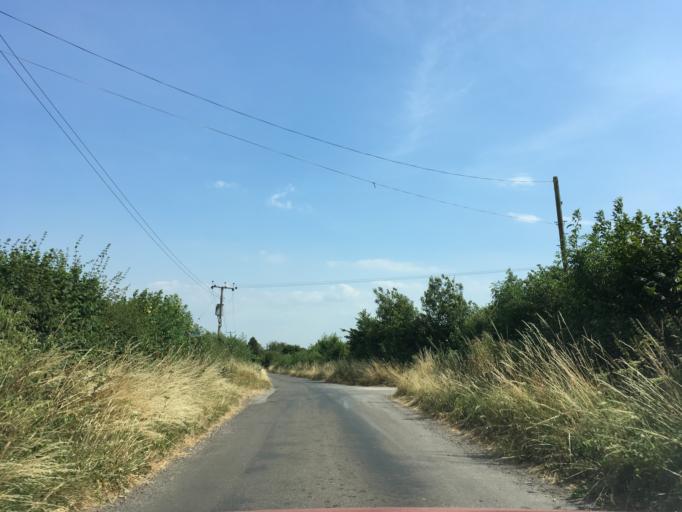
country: GB
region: England
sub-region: South Gloucestershire
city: Tytherington
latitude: 51.5794
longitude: -2.5036
